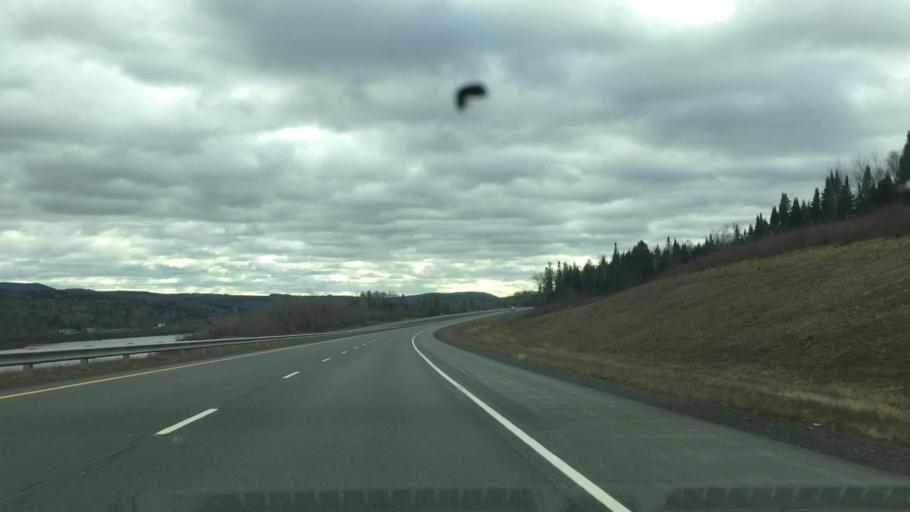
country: US
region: Maine
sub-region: Aroostook County
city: Fort Fairfield
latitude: 46.6793
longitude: -67.7311
